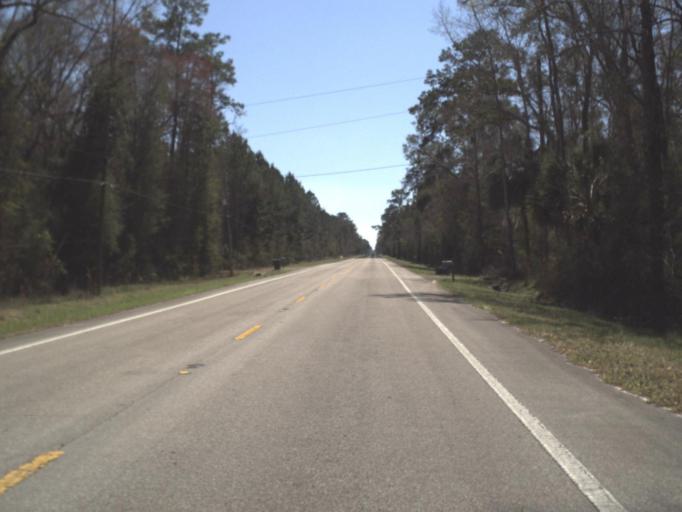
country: US
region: Florida
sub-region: Leon County
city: Woodville
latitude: 30.2272
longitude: -84.2281
